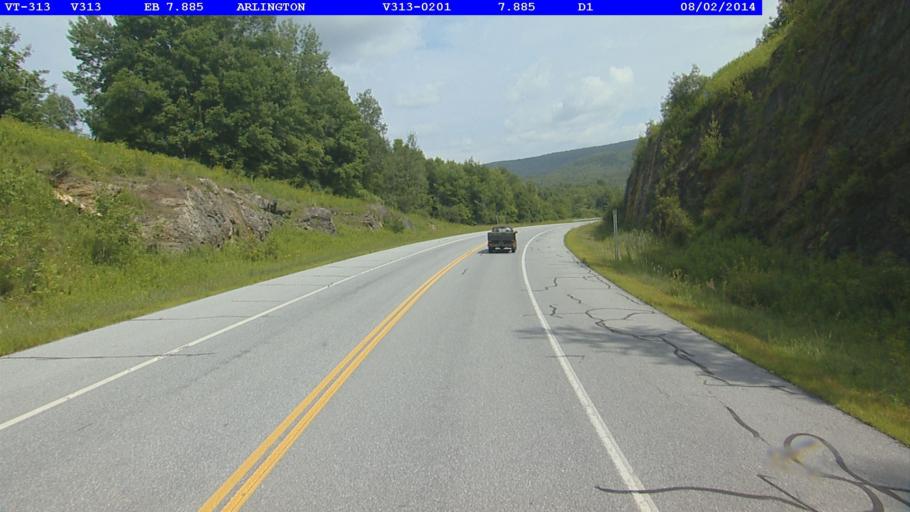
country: US
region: Vermont
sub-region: Bennington County
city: Arlington
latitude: 43.0534
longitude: -73.1394
